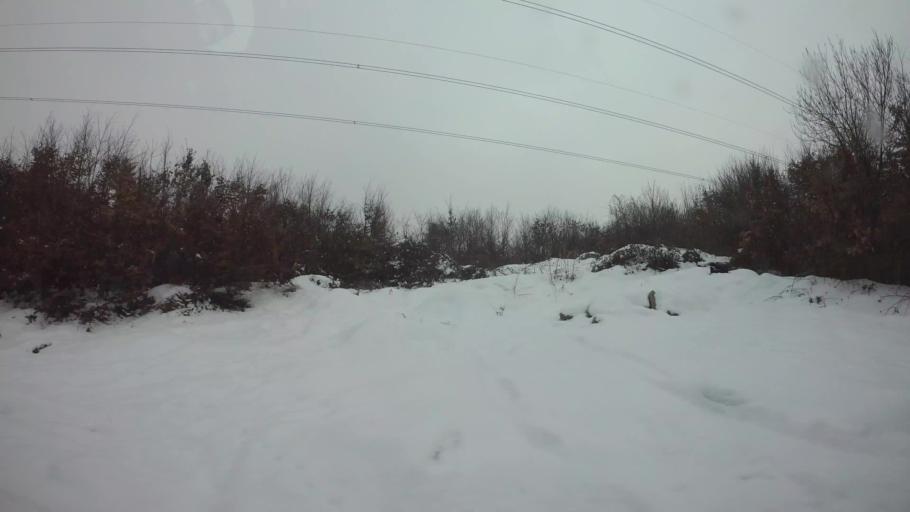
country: BA
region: Federation of Bosnia and Herzegovina
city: Hadzici
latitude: 43.8441
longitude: 18.2683
